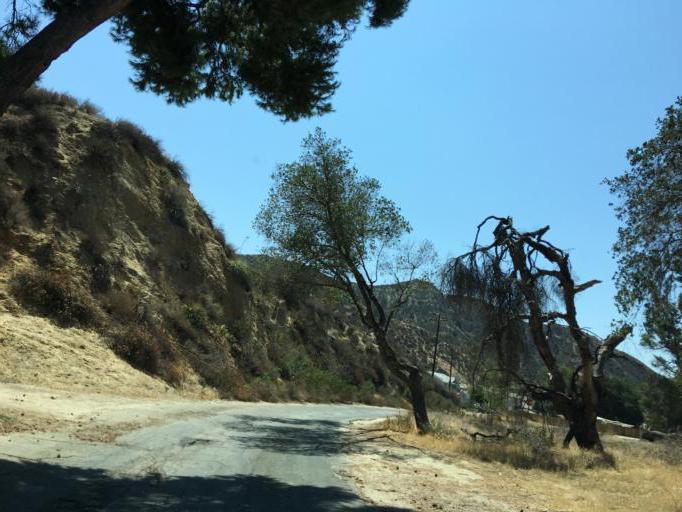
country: US
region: California
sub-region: Los Angeles County
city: Val Verde
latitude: 34.4440
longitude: -118.6560
